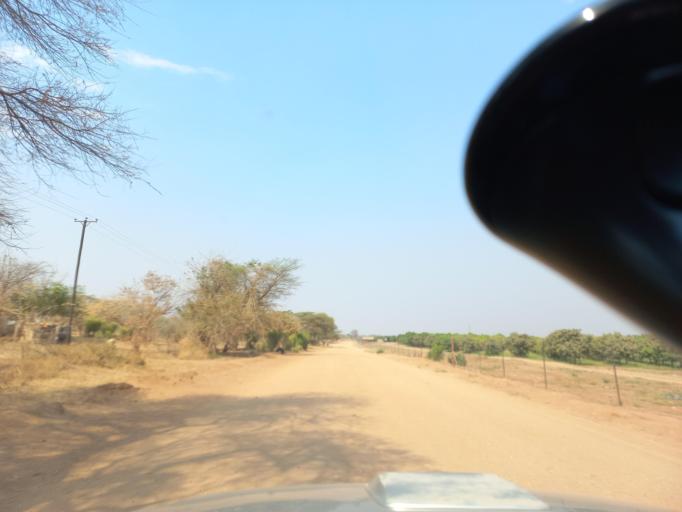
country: ZW
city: Chirundu
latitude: -15.9328
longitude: 28.9480
